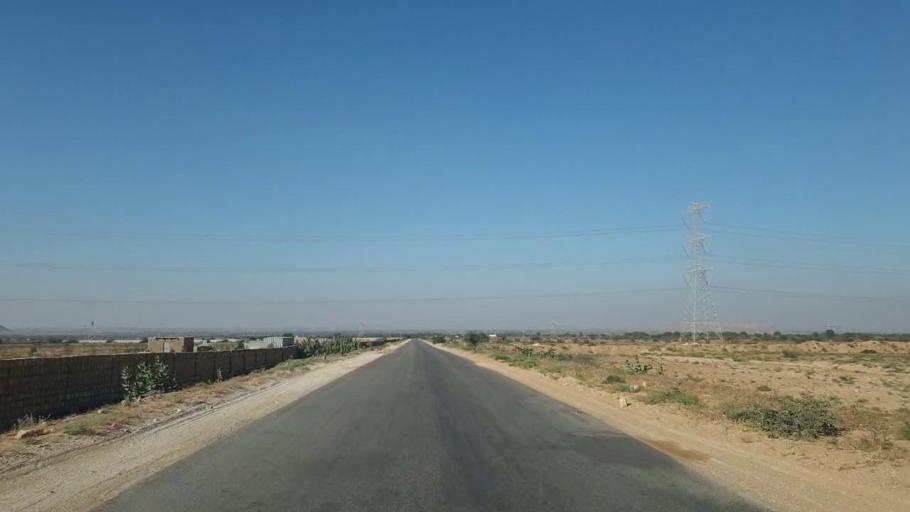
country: PK
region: Sindh
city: Gharo
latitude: 25.1785
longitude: 67.6590
